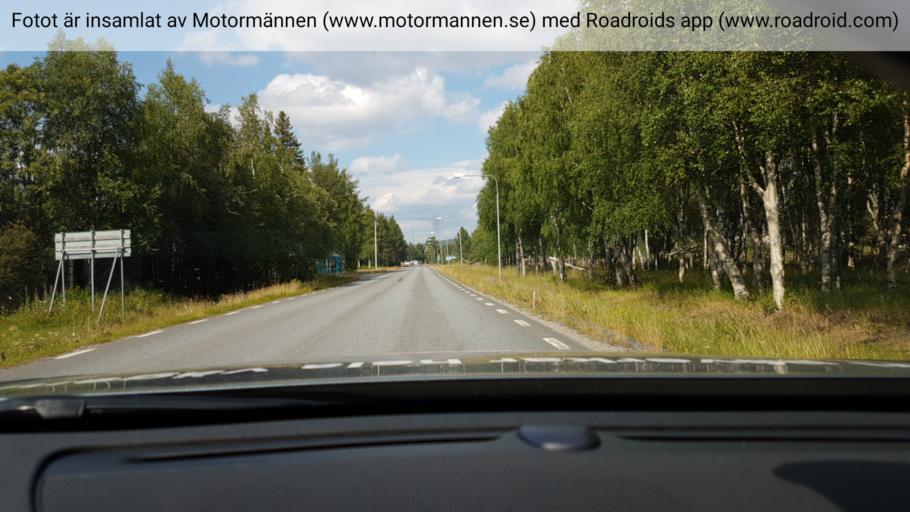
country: SE
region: Vaesterbotten
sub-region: Sorsele Kommun
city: Sorsele
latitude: 65.5260
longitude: 17.5392
